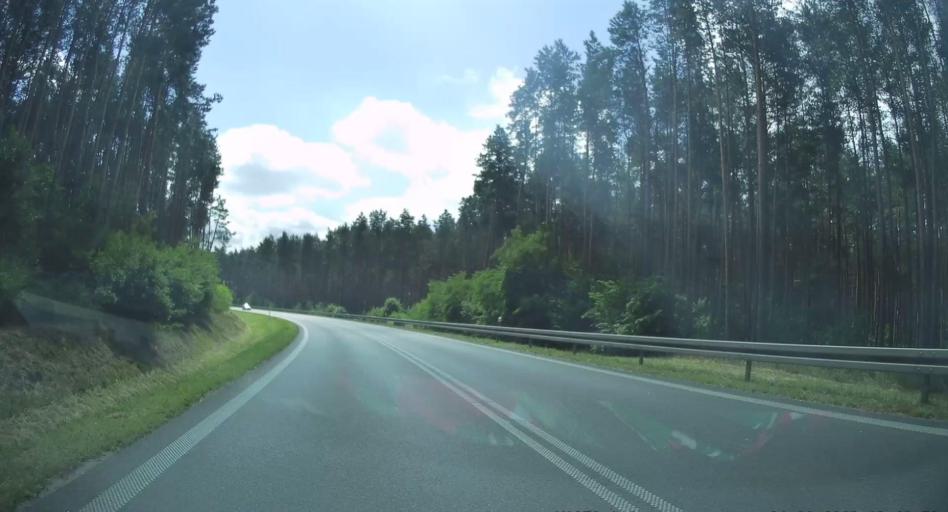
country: PL
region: Subcarpathian Voivodeship
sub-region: Powiat mielecki
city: Padew Narodowa
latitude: 50.3593
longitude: 21.4835
